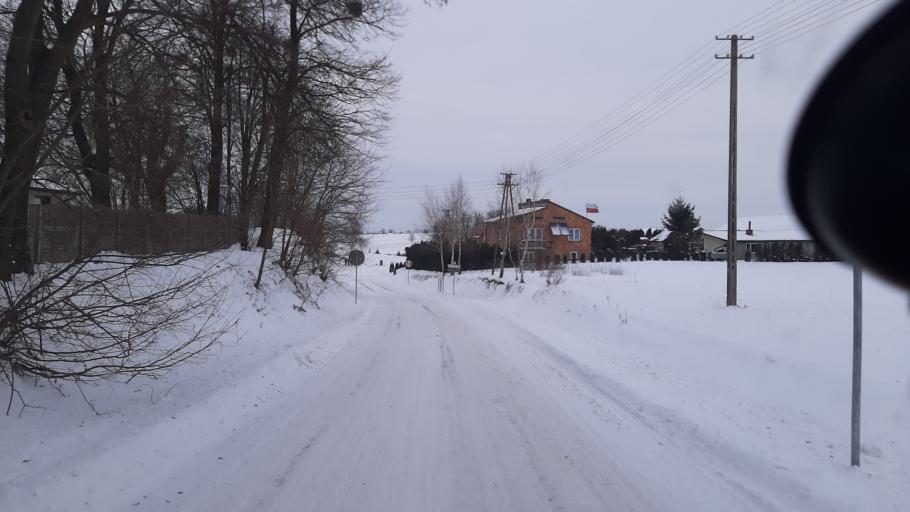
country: PL
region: Lublin Voivodeship
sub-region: Powiat lubelski
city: Garbow
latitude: 51.3338
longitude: 22.2918
